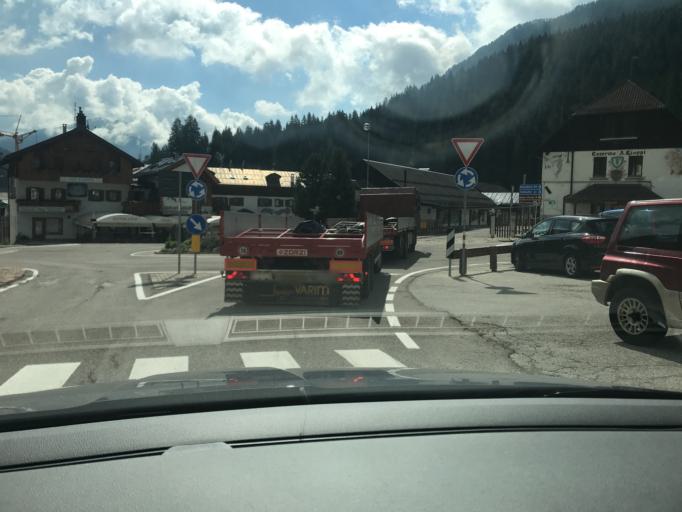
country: IT
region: Trentino-Alto Adige
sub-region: Bolzano
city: Corvara in Badia
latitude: 46.4973
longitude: 11.8743
